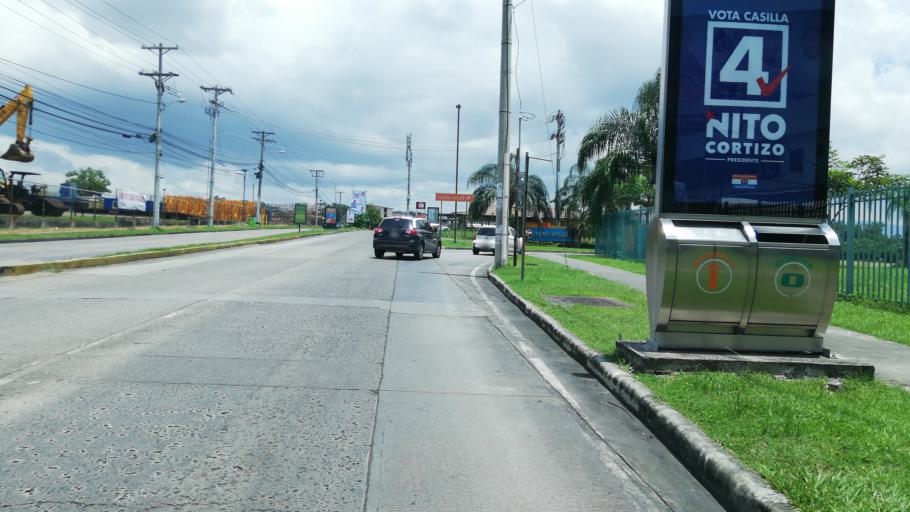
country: PA
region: Panama
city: San Miguelito
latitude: 9.0514
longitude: -79.4542
